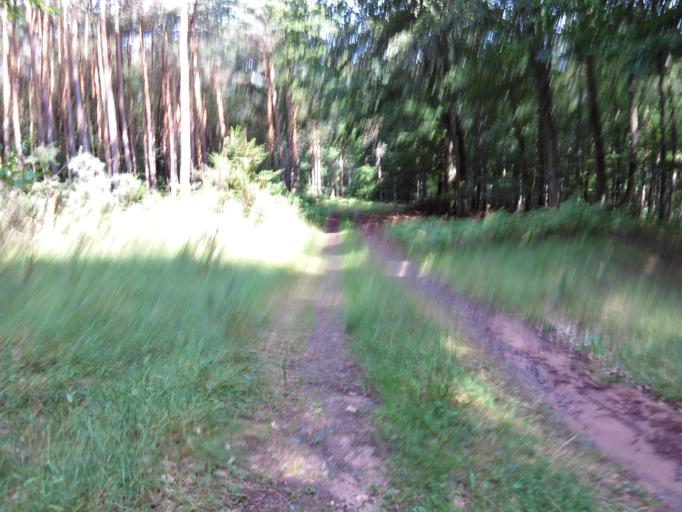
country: DE
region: Rheinland-Pfalz
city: Neidenfels
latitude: 49.4229
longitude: 8.0713
